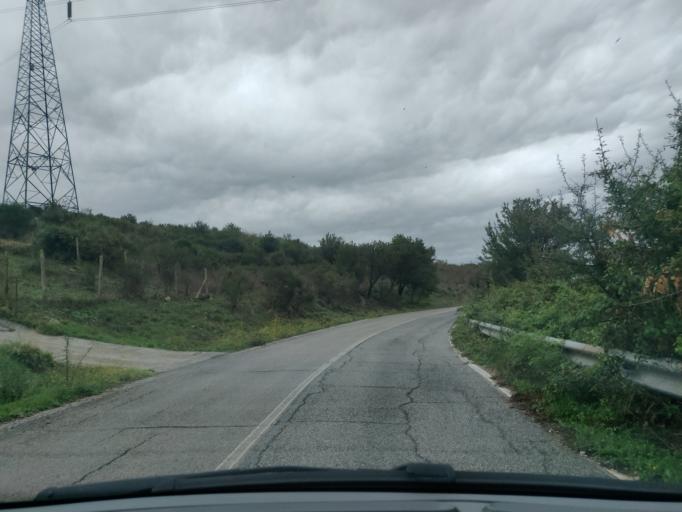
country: IT
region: Latium
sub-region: Citta metropolitana di Roma Capitale
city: Aurelia
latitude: 42.1322
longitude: 11.8414
